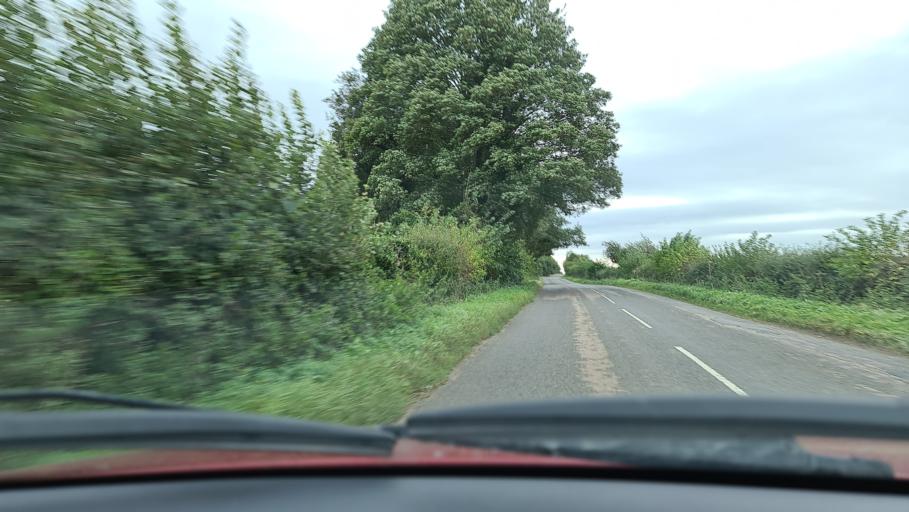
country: GB
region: England
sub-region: Oxfordshire
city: Adderbury
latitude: 52.0114
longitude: -1.2731
